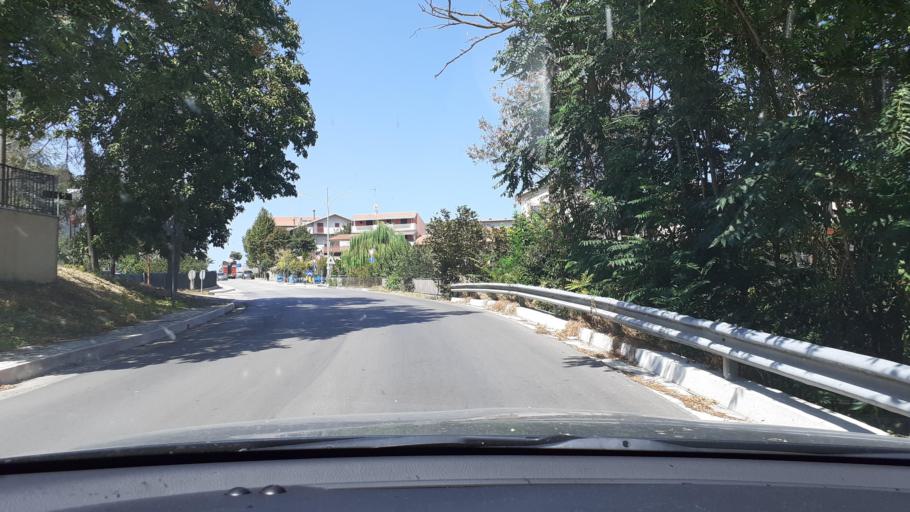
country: IT
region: Abruzzo
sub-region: Provincia di Chieti
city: Santa Maria Imbaro
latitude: 42.2203
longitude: 14.4512
